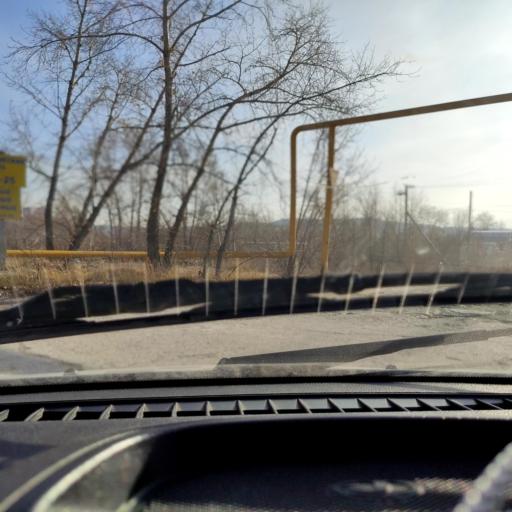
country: RU
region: Samara
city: Zhigulevsk
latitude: 53.4635
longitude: 49.5568
